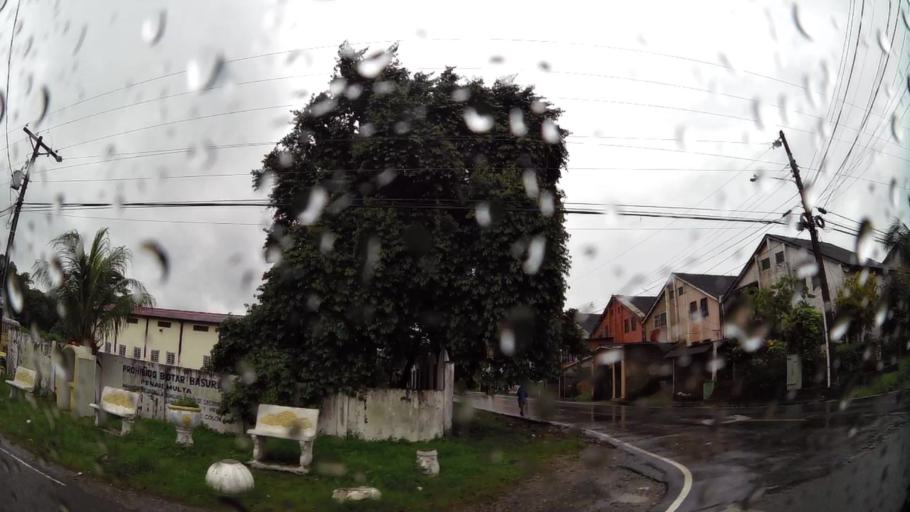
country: PA
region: Colon
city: Arco Iris
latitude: 9.3363
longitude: -79.8735
